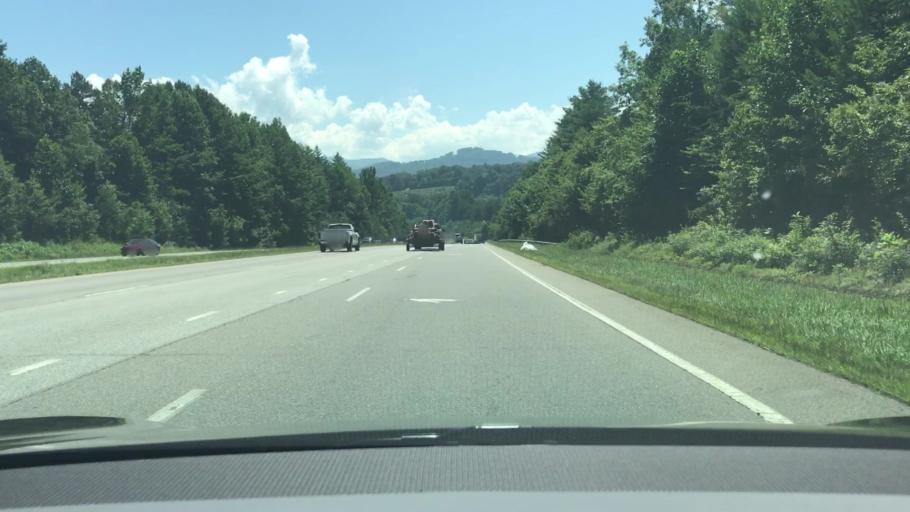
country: US
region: North Carolina
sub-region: Macon County
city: Franklin
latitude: 35.1650
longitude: -83.3836
